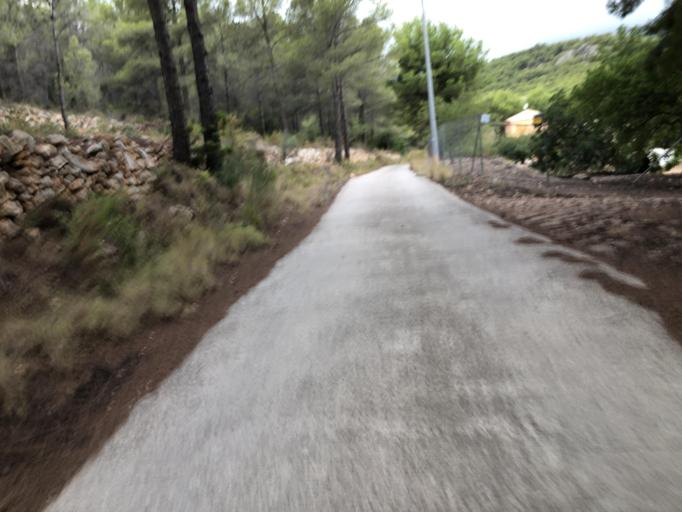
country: ES
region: Valencia
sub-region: Provincia de Alicante
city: Polop
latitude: 38.6393
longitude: -0.1349
